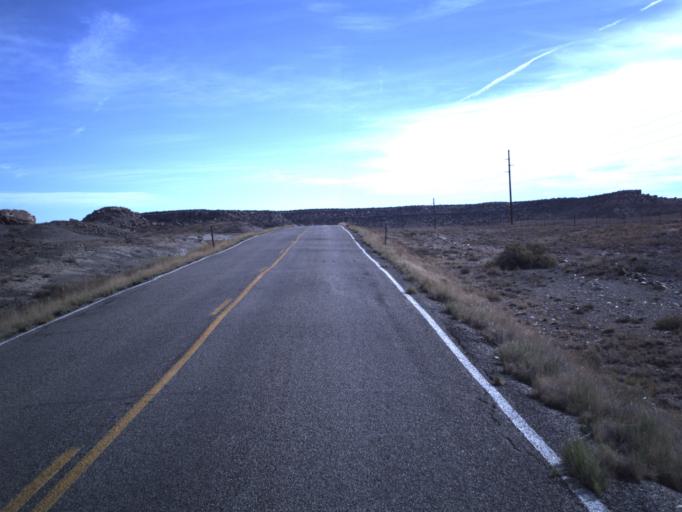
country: US
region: Utah
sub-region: San Juan County
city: Blanding
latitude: 37.4187
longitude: -109.4276
